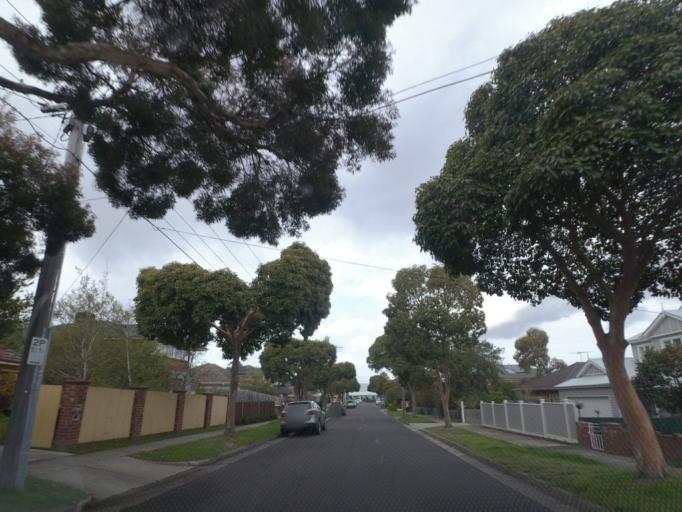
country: AU
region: Victoria
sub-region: Whitehorse
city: Blackburn
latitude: -37.8162
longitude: 145.1548
